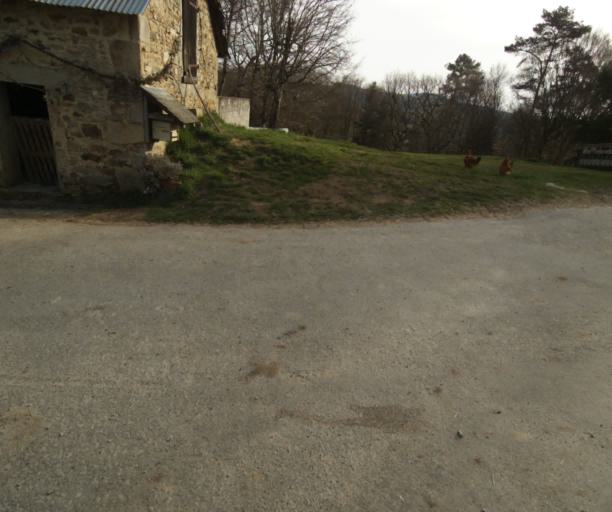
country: FR
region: Limousin
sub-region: Departement de la Correze
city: Chamboulive
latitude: 45.4421
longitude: 1.7451
